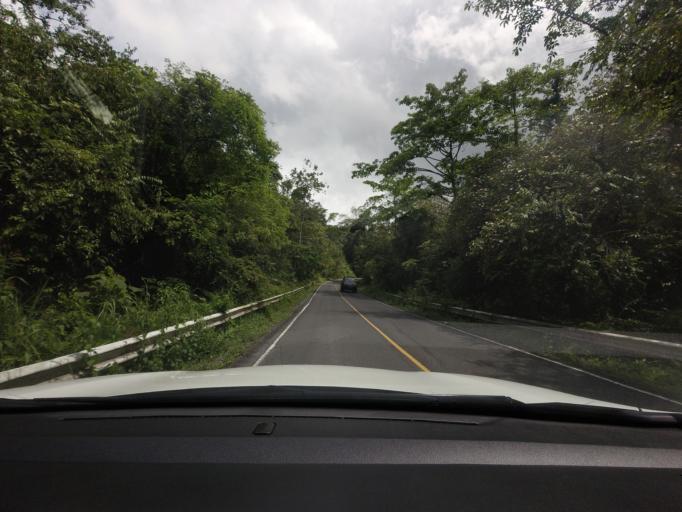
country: TH
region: Nakhon Nayok
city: Nakhon Nayok
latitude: 14.3486
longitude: 101.3438
